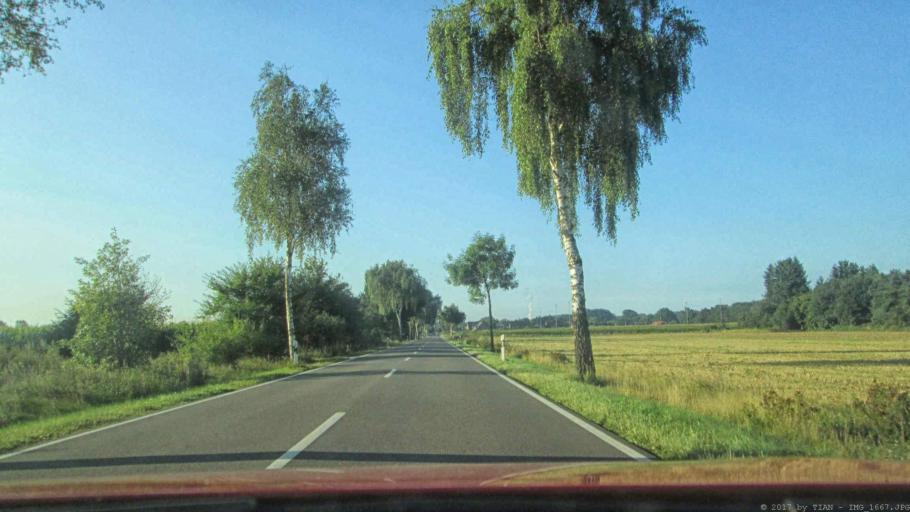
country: DE
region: Lower Saxony
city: Barwedel
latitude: 52.5775
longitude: 10.7873
